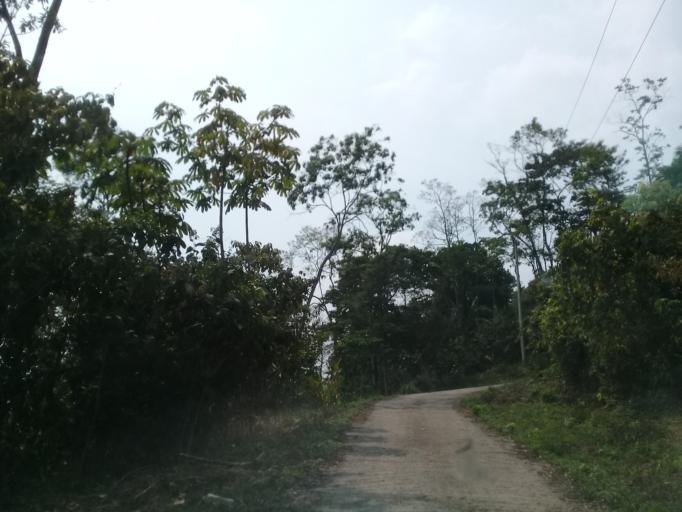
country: MX
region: Veracruz
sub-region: Tezonapa
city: Laguna Chica (Pueblo Nuevo)
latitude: 18.5819
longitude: -96.7519
